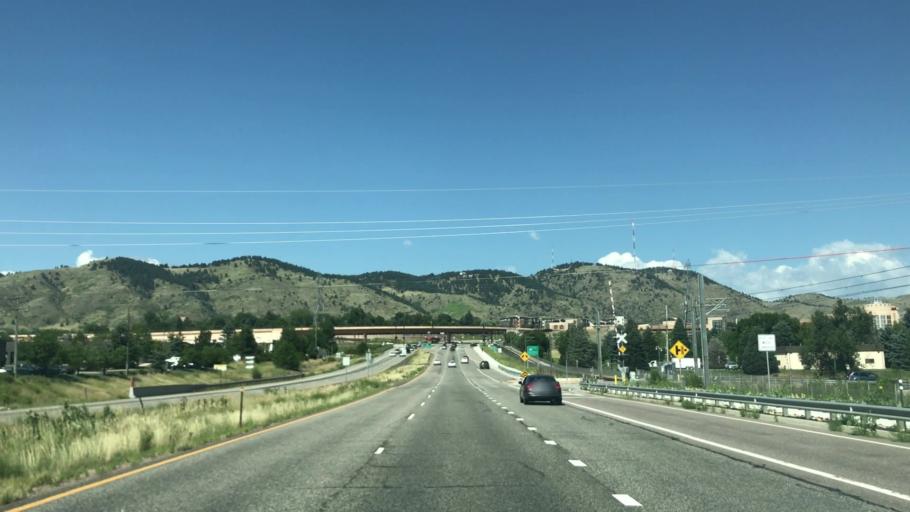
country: US
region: Colorado
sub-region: Jefferson County
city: West Pleasant View
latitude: 39.7252
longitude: -105.1931
